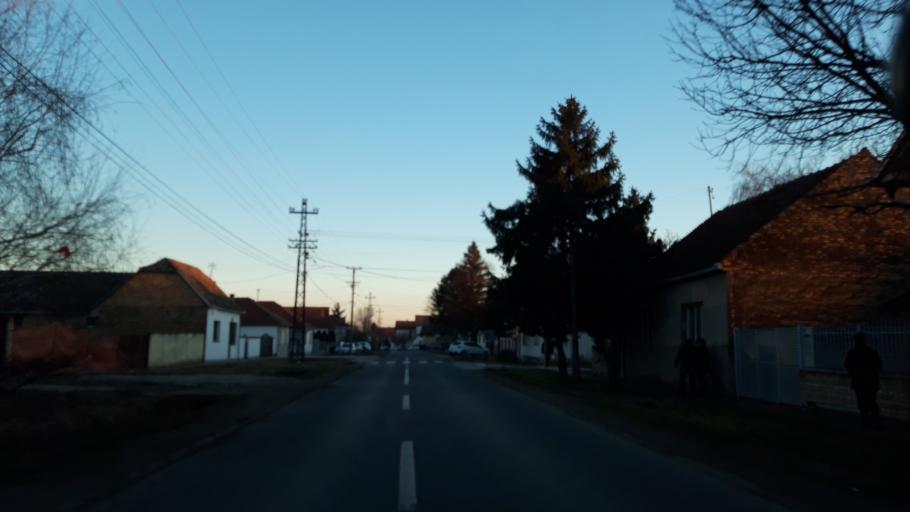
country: RS
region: Autonomna Pokrajina Vojvodina
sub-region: Sremski Okrug
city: Ingija
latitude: 45.0488
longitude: 20.0691
